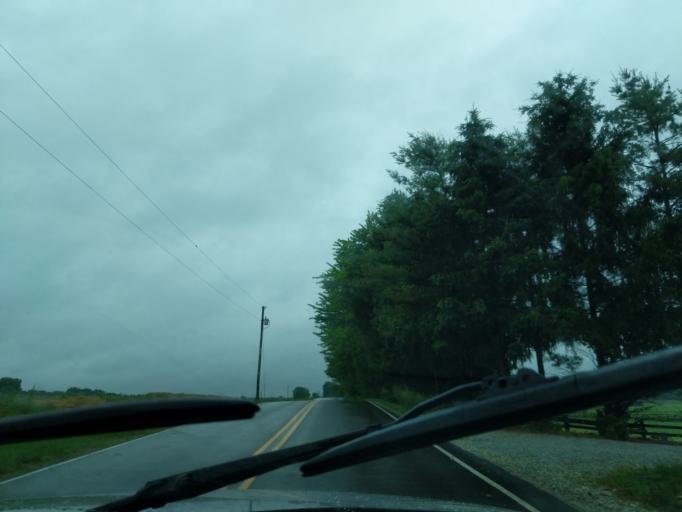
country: US
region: Indiana
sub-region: Madison County
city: Lapel
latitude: 40.0669
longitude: -85.8964
